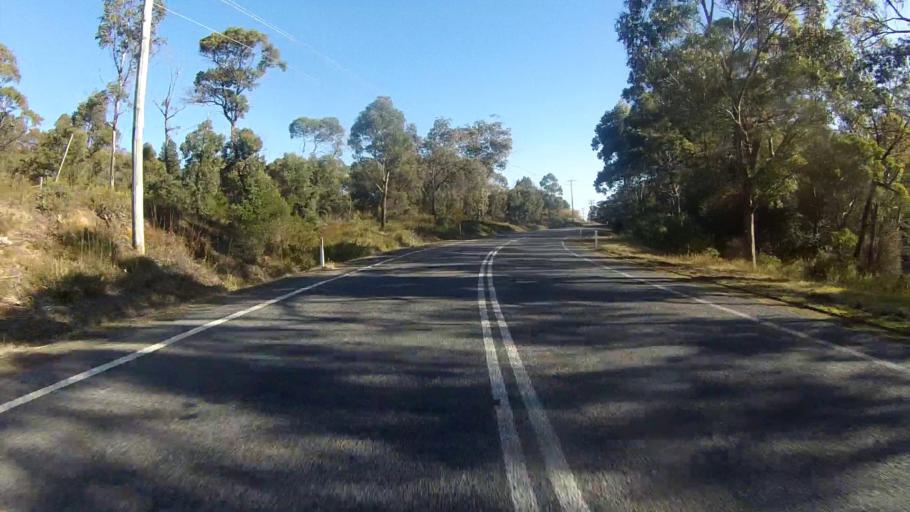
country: AU
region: Tasmania
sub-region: Clarence
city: Sandford
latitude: -43.0231
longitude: 147.8966
